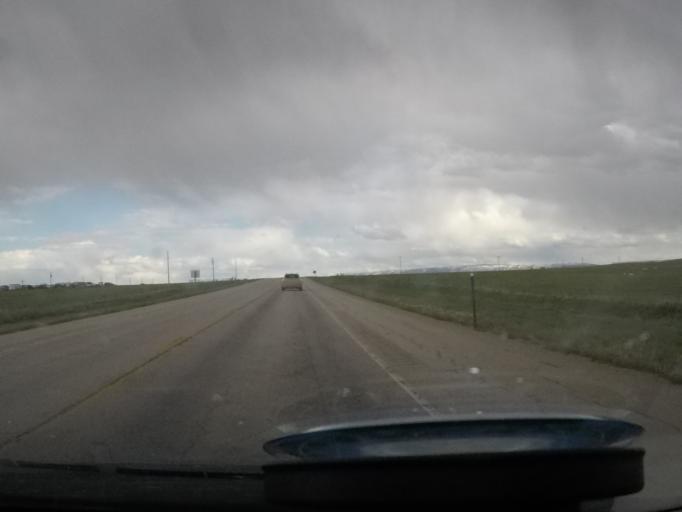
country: US
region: Wyoming
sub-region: Natrona County
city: Mills
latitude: 42.9573
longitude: -106.6518
